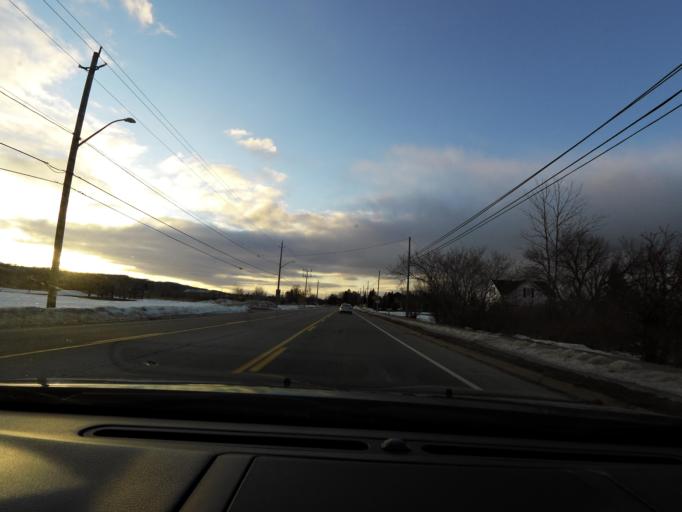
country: CA
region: Ontario
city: Hamilton
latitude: 43.2054
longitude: -79.6214
